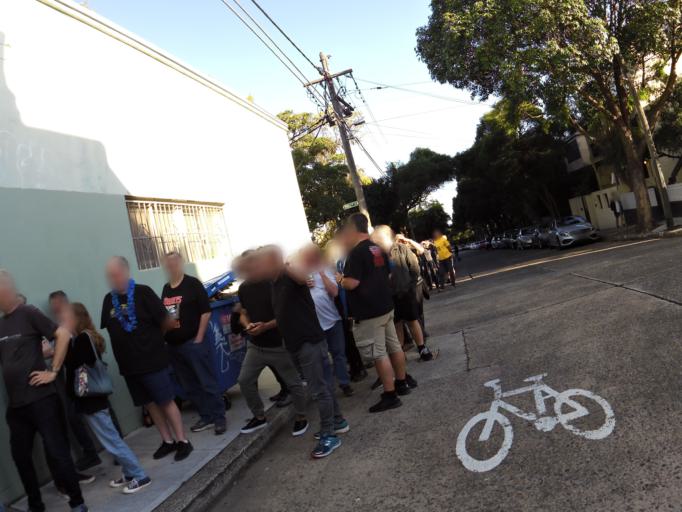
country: AU
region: New South Wales
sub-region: Marrickville
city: Newtown
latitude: -33.8991
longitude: 151.1737
